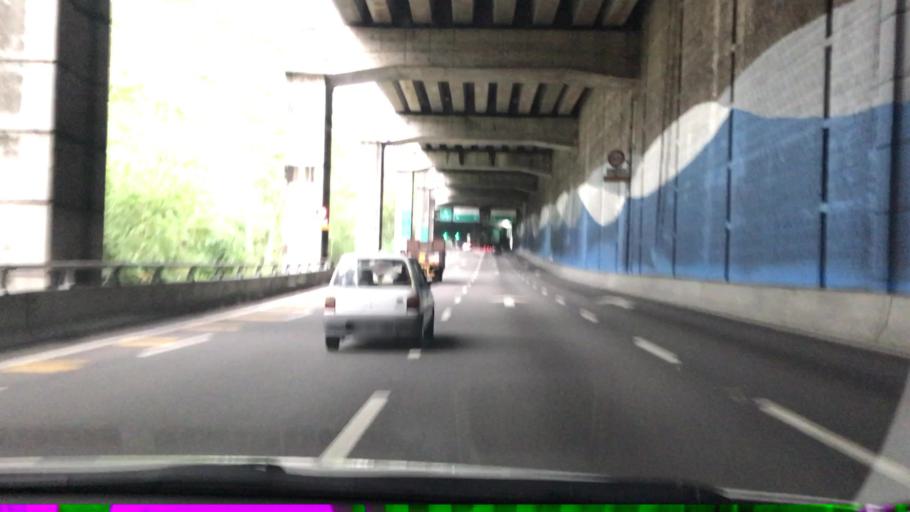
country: MY
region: Kuala Lumpur
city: Kuala Lumpur
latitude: 3.1256
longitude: 101.6619
